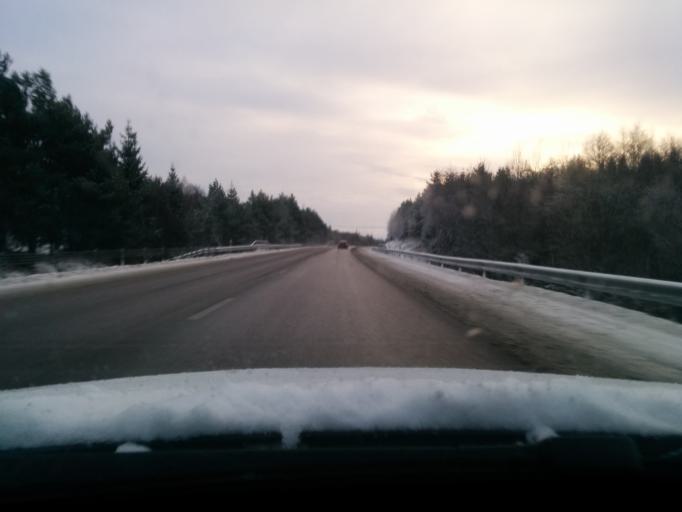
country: SE
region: Uppsala
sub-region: Knivsta Kommun
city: Knivsta
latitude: 59.7018
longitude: 17.8581
